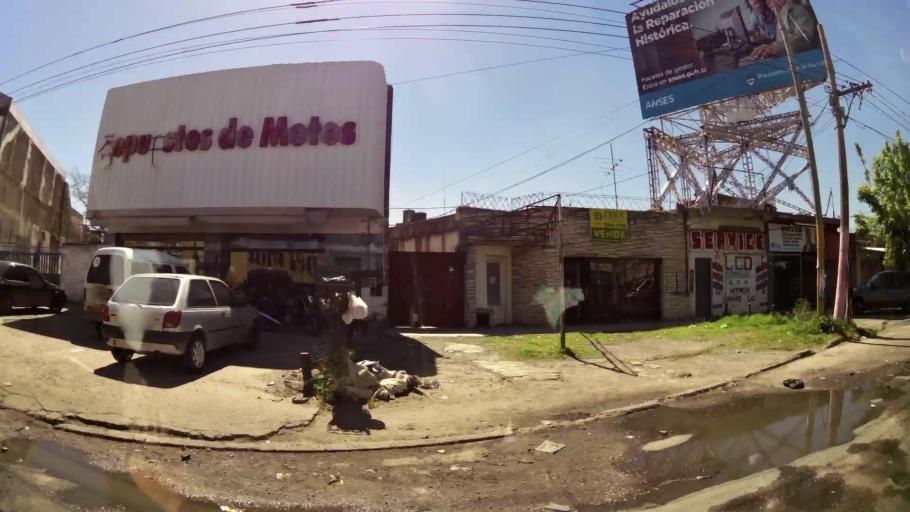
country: AR
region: Buenos Aires
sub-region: Partido de Quilmes
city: Quilmes
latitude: -34.7166
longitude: -58.3046
